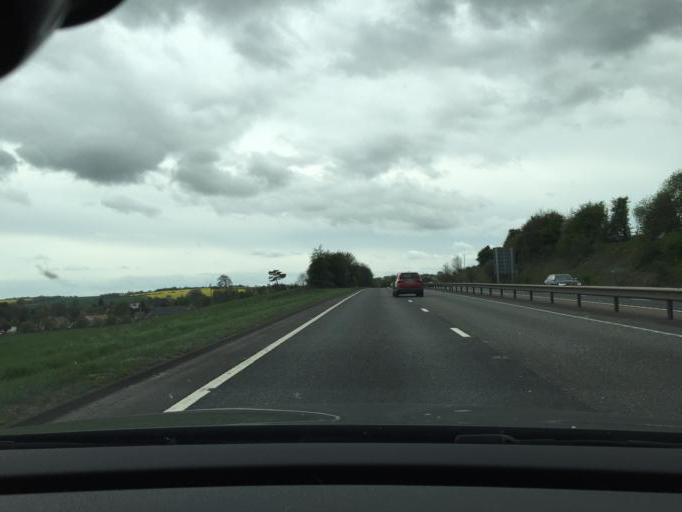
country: GB
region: England
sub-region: Oxfordshire
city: Harwell
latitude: 51.5327
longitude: -1.2941
